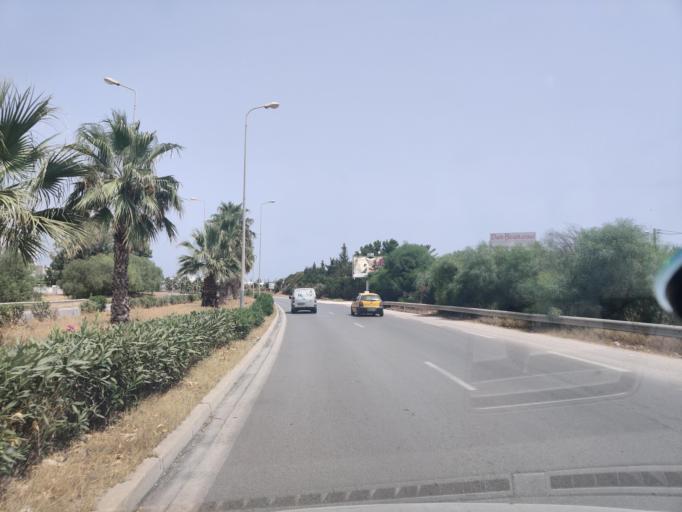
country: TN
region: Tunis
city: Carthage
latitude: 36.8610
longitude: 10.3152
